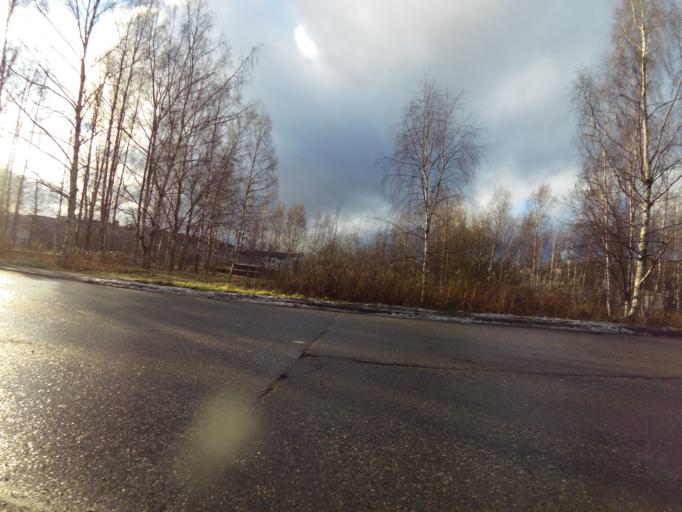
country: FI
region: Uusimaa
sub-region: Helsinki
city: Koukkuniemi
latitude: 60.1816
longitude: 24.7618
